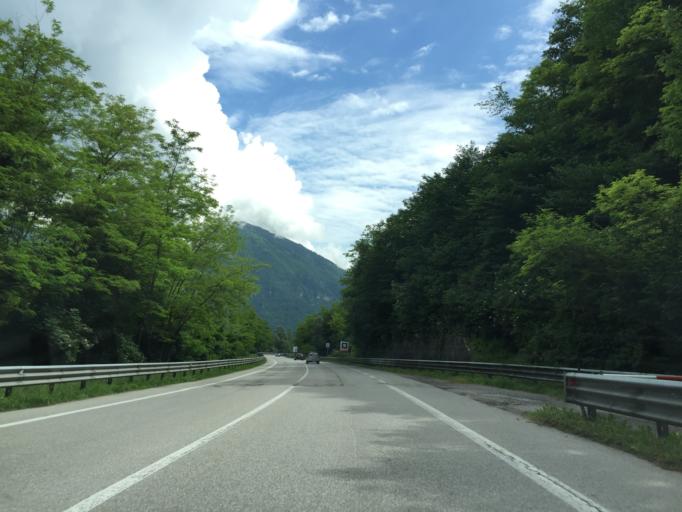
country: IT
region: Veneto
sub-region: Provincia di Belluno
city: Fonzaso
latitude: 45.9907
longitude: 11.7901
